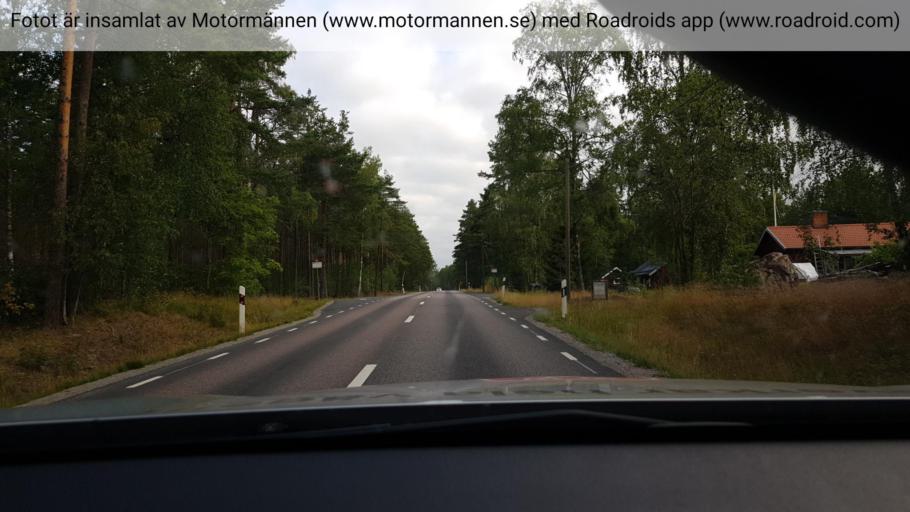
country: SE
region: Stockholm
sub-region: Norrtalje Kommun
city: Rimbo
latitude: 59.7828
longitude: 18.4369
